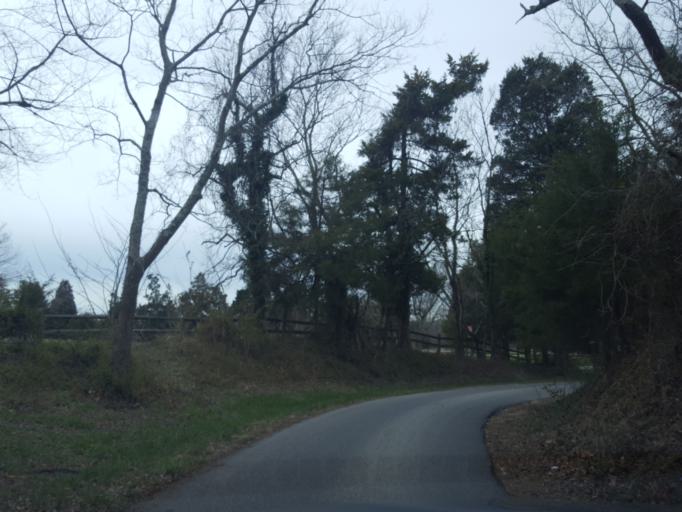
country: US
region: Maryland
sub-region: Calvert County
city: Lusby
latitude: 38.3991
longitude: -76.5072
